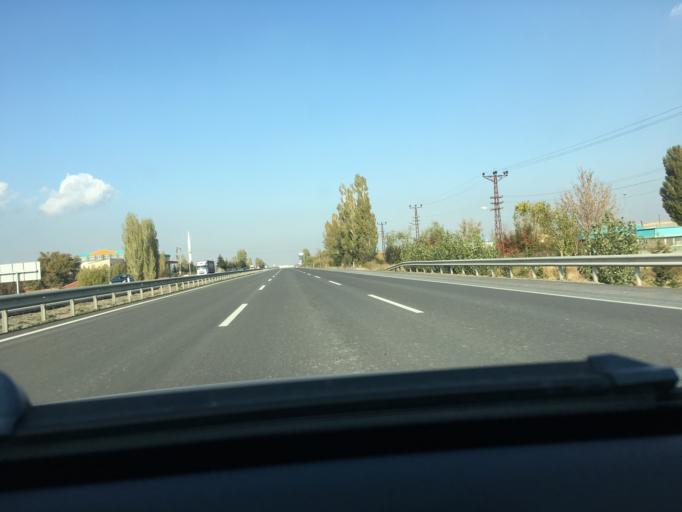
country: TR
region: Ankara
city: Polatli
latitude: 39.6680
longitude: 32.2286
